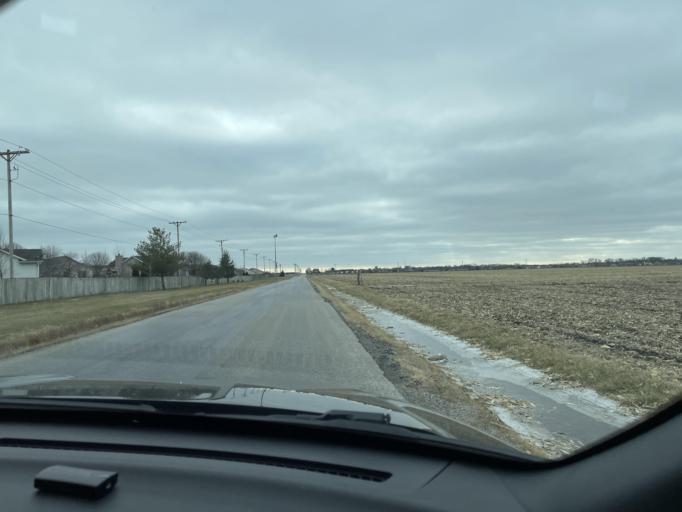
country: US
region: Illinois
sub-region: Sangamon County
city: Jerome
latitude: 39.7752
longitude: -89.7535
